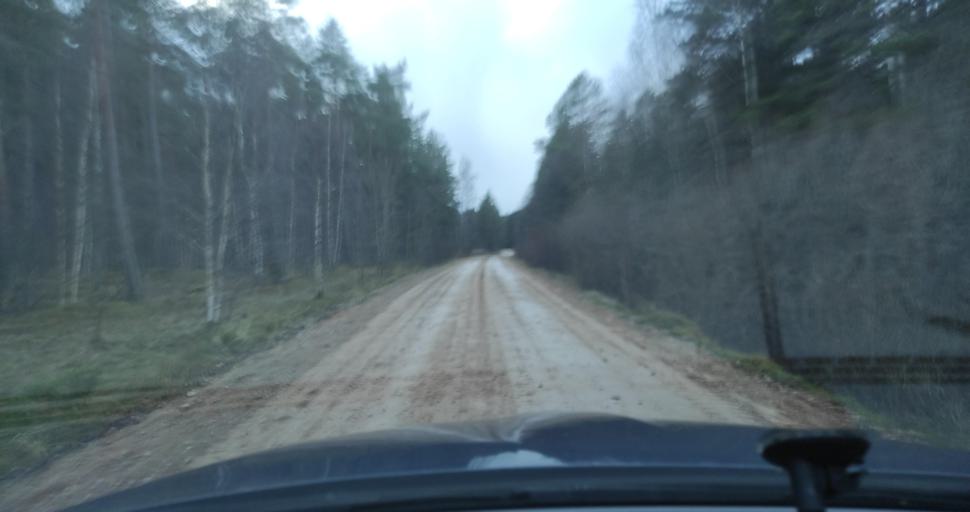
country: LV
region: Pavilostas
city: Pavilosta
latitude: 56.8384
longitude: 21.0793
